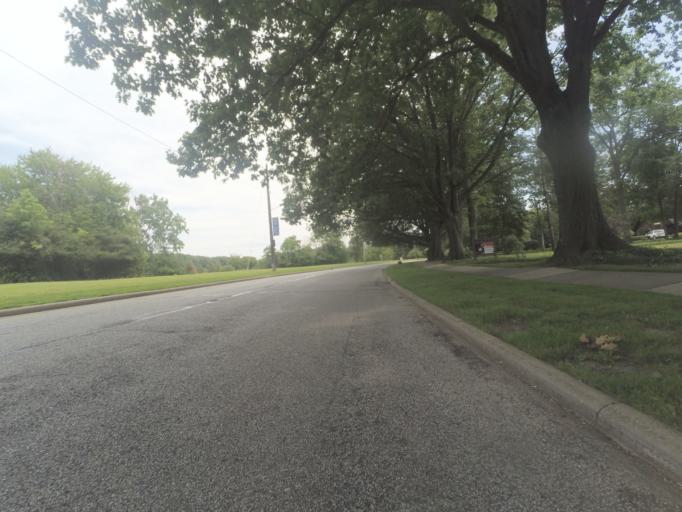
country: US
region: Ohio
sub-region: Cuyahoga County
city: Shaker Heights
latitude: 41.4827
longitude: -81.5625
